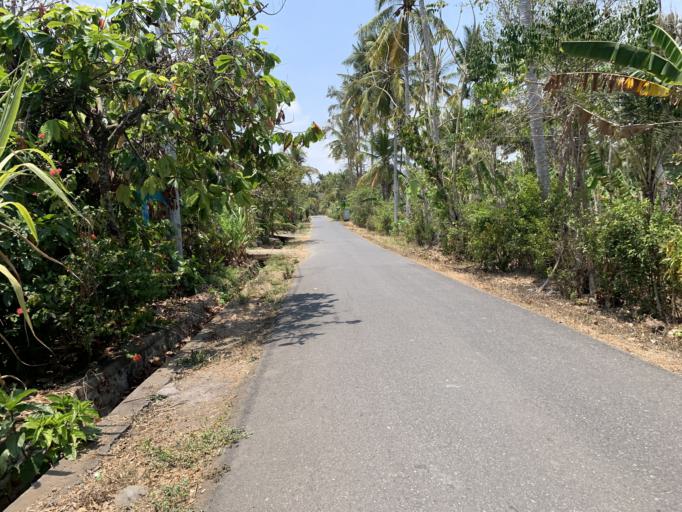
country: ID
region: Bali
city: Banjar Dangin Pangkung
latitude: -8.4321
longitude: 114.8375
